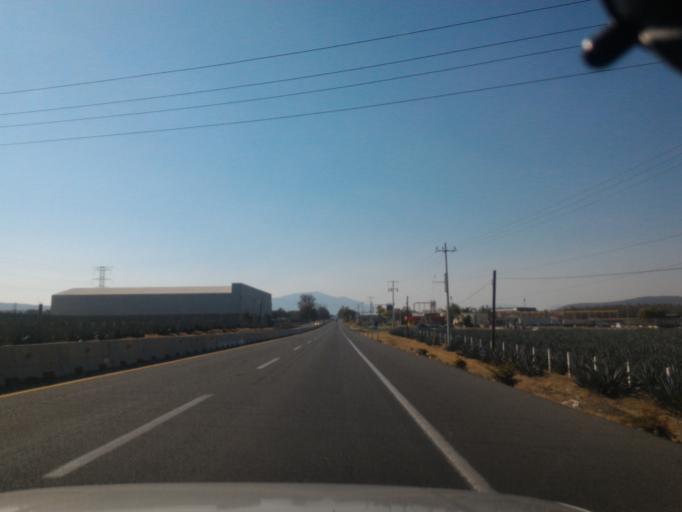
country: MX
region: Jalisco
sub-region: Poncitlan
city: Santa Cruz el Grande
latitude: 20.3654
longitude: -102.8362
